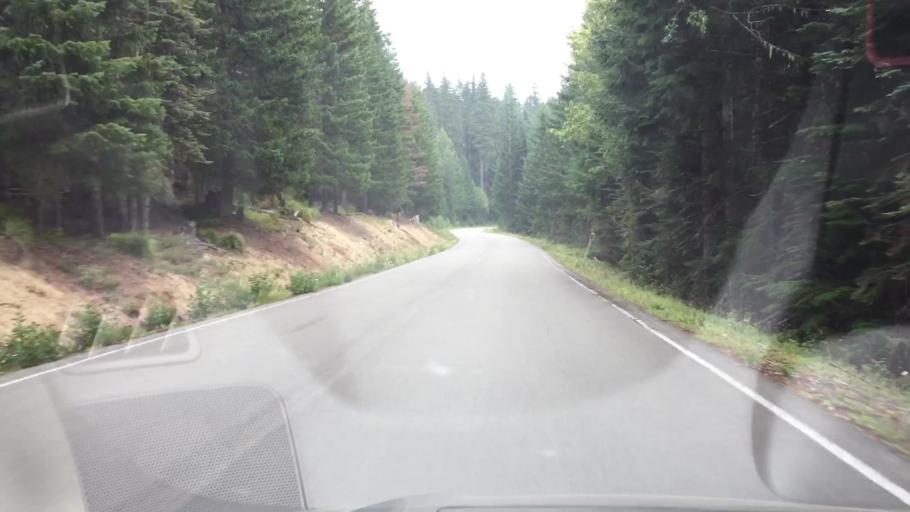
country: US
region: Washington
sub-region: Klickitat County
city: White Salmon
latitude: 46.1818
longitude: -121.6397
